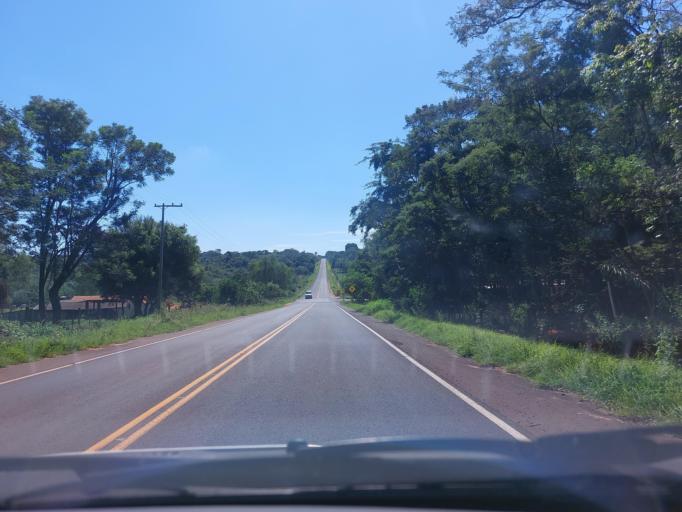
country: PY
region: San Pedro
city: Guayaybi
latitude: -24.5511
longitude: -56.5196
